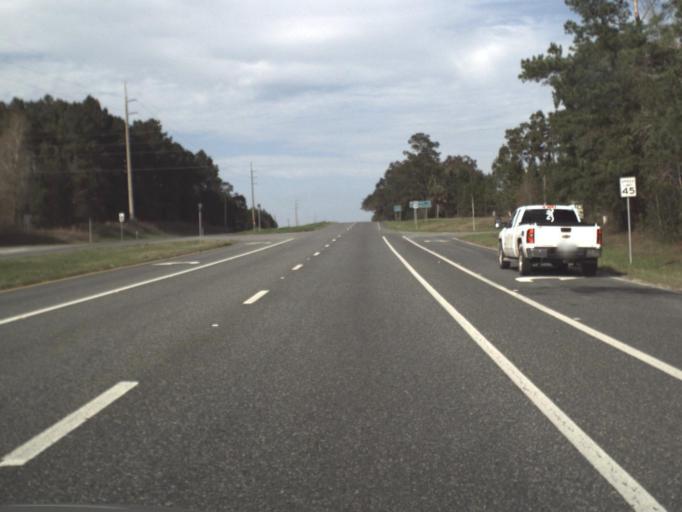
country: US
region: Florida
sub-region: Jefferson County
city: Monticello
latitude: 30.4776
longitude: -83.8885
